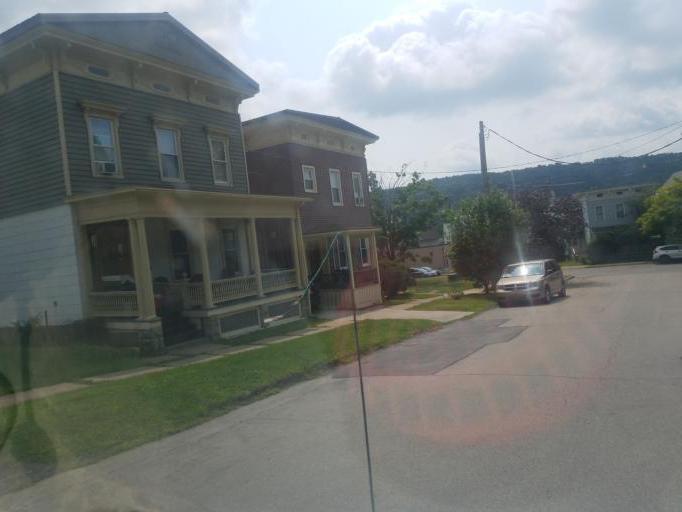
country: US
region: New York
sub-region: Herkimer County
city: Little Falls
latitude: 43.0453
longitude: -74.8547
